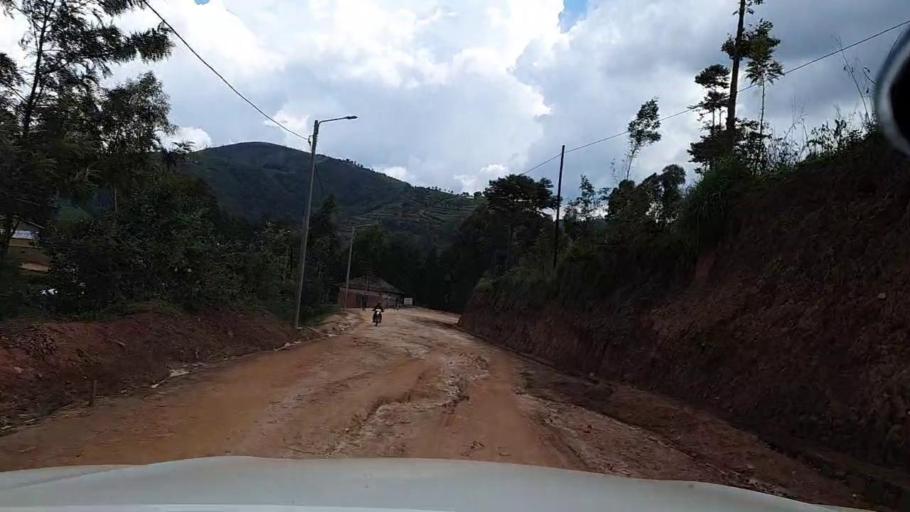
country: RW
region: Southern Province
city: Nzega
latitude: -2.6936
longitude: 29.4436
